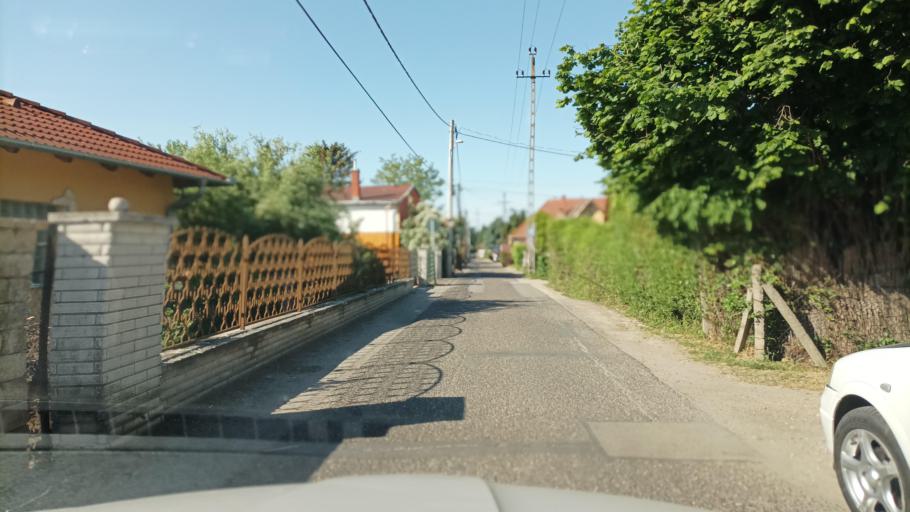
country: HU
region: Pest
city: Szigetszentmiklos
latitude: 47.3450
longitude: 19.0536
